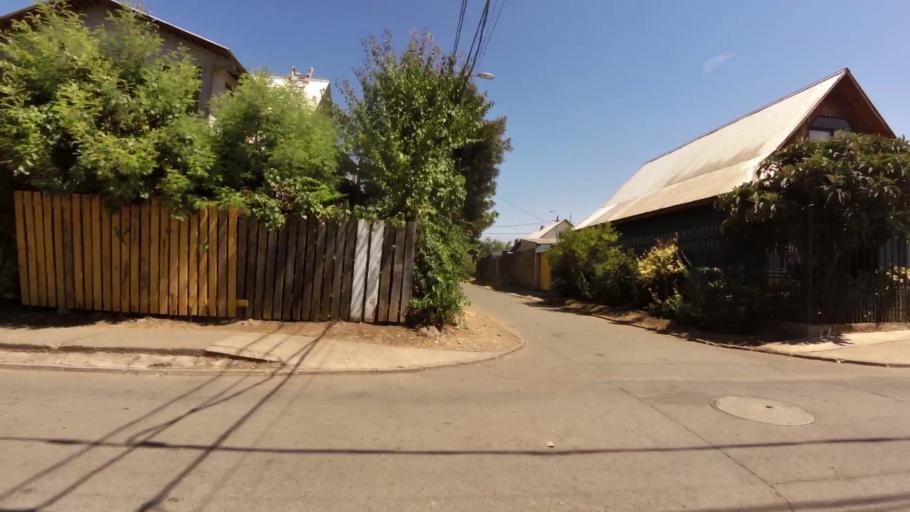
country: CL
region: Maule
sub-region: Provincia de Curico
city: Curico
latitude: -34.9767
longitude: -71.2175
